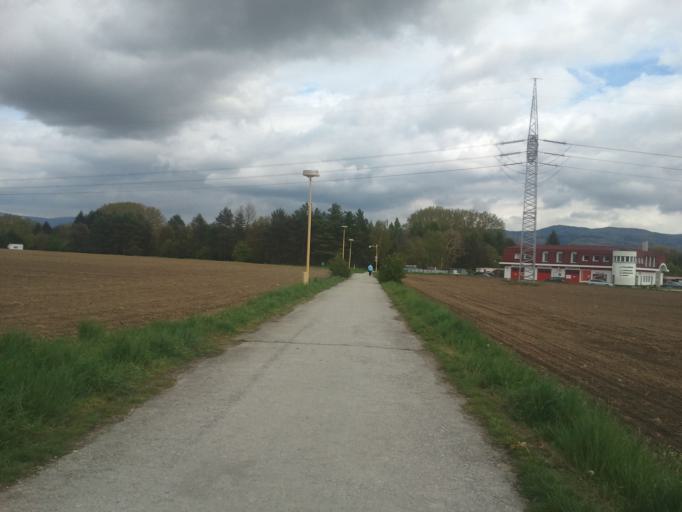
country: SK
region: Nitriansky
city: Bojnice
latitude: 48.7774
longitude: 18.5900
